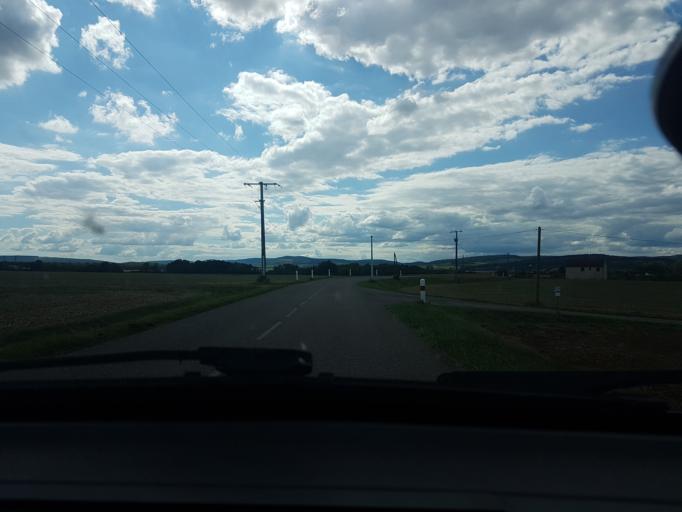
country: FR
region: Bourgogne
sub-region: Departement de Saone-et-Loire
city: Fontaines
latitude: 46.8430
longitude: 4.7947
